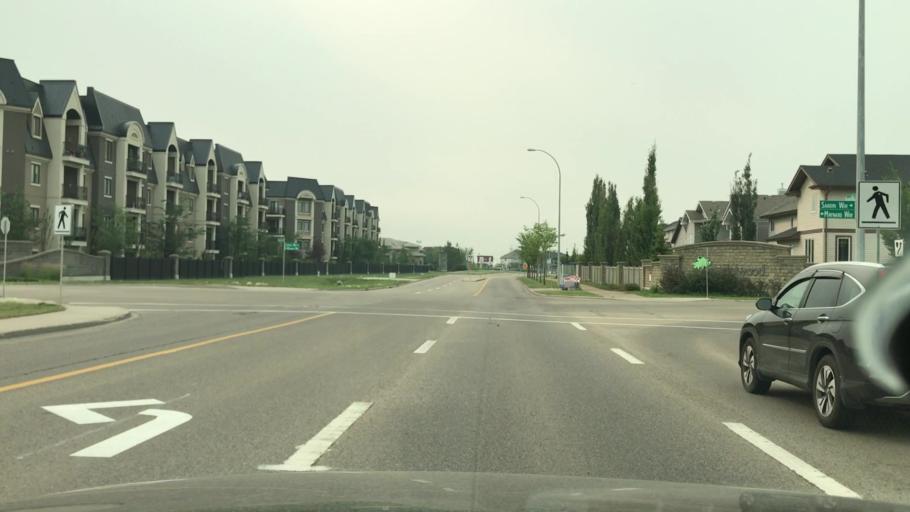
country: CA
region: Alberta
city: Edmonton
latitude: 53.4417
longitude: -113.5657
